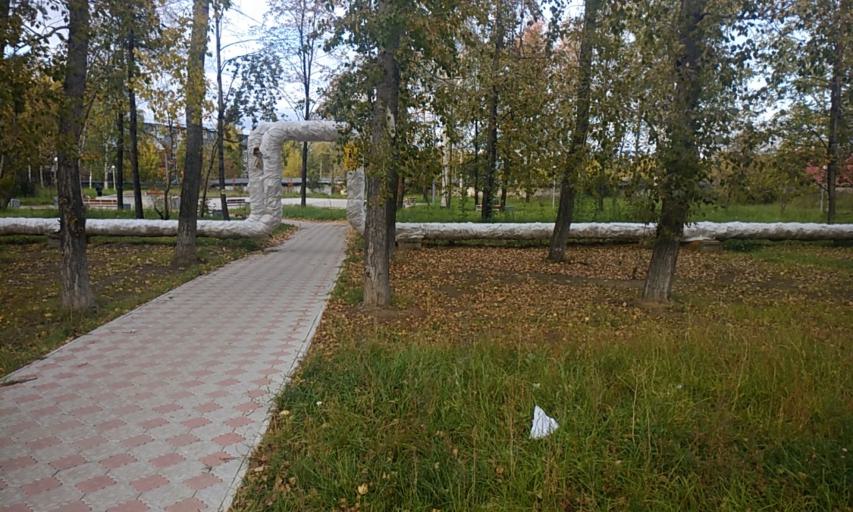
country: RU
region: Sverdlovsk
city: Krasnoural'sk
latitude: 58.3560
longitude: 60.0426
